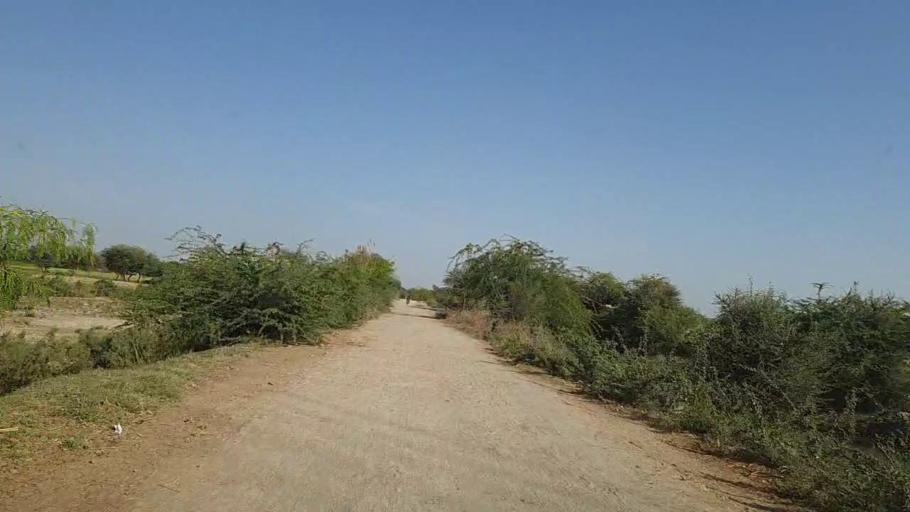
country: PK
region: Sindh
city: Kotri
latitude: 25.1630
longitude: 68.2986
